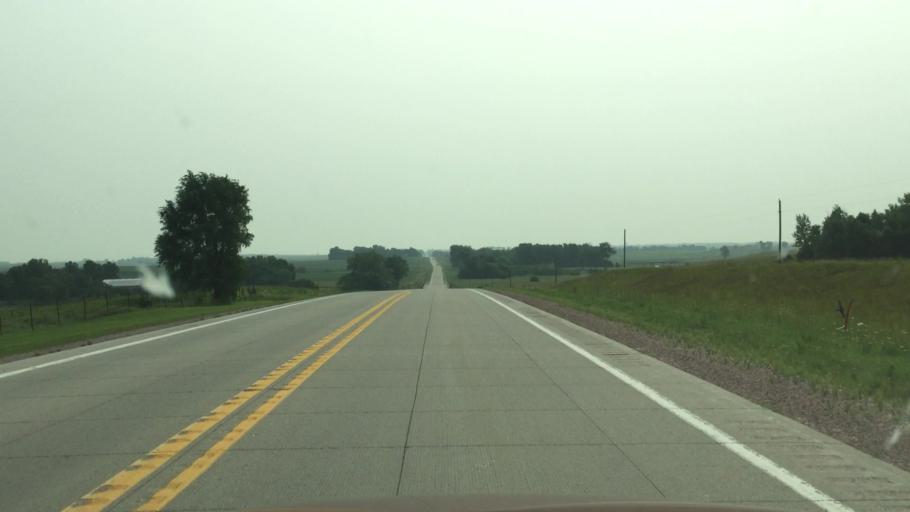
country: US
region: Iowa
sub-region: Osceola County
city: Sibley
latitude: 43.4330
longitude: -95.6178
